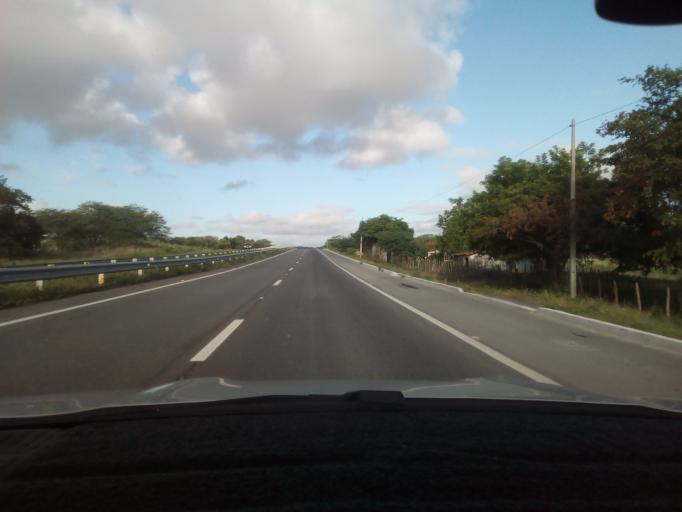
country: BR
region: Paraiba
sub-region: Mogeiro
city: Mogeiro
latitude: -7.2050
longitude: -35.5102
